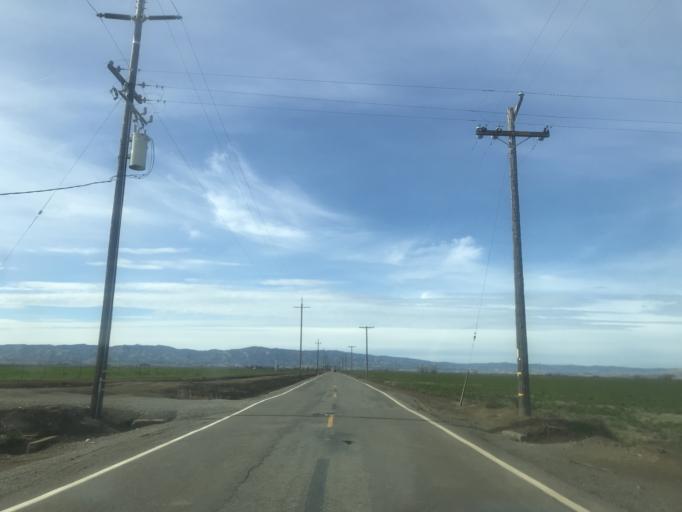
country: US
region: California
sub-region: Yolo County
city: Cottonwood
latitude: 38.6638
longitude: -121.9152
